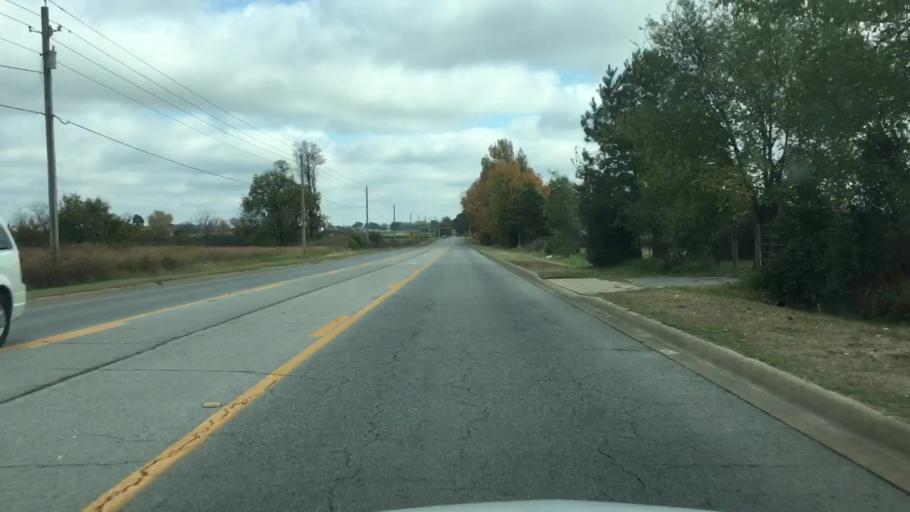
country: US
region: Arkansas
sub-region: Benton County
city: Siloam Springs
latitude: 36.1953
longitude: -94.5019
